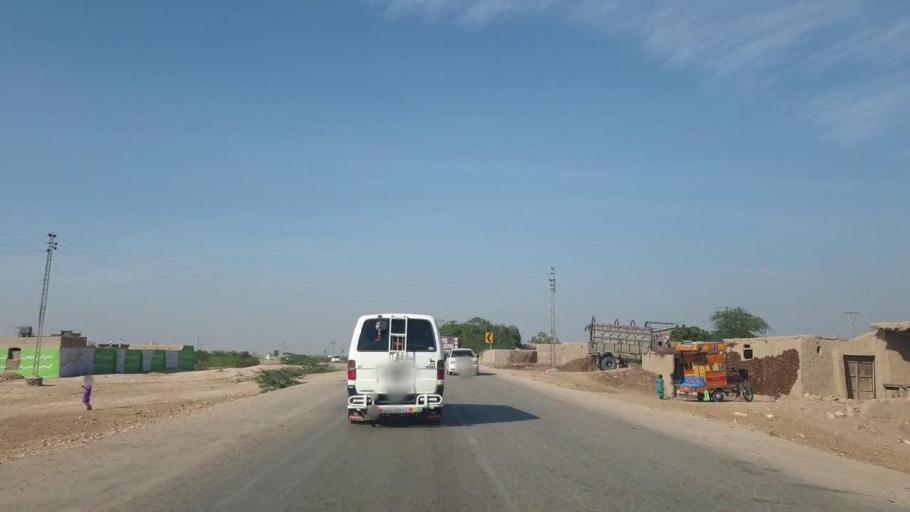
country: PK
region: Sindh
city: Sehwan
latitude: 26.3855
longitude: 67.8709
